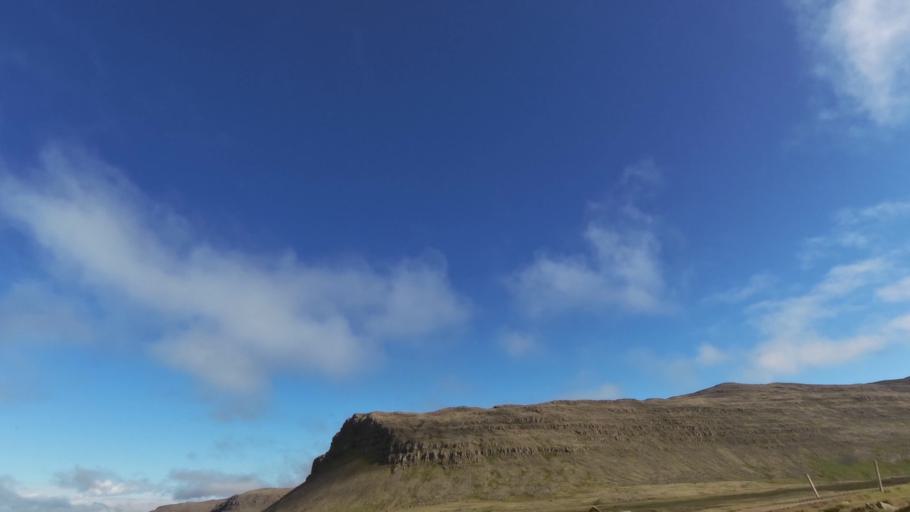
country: IS
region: West
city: Olafsvik
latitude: 65.5727
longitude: -24.0634
